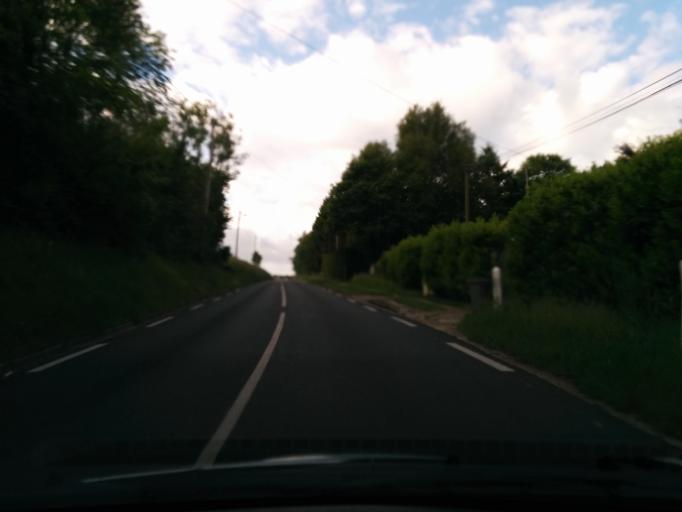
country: FR
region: Haute-Normandie
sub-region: Departement de l'Eure
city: Gasny
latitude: 49.0826
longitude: 1.6120
